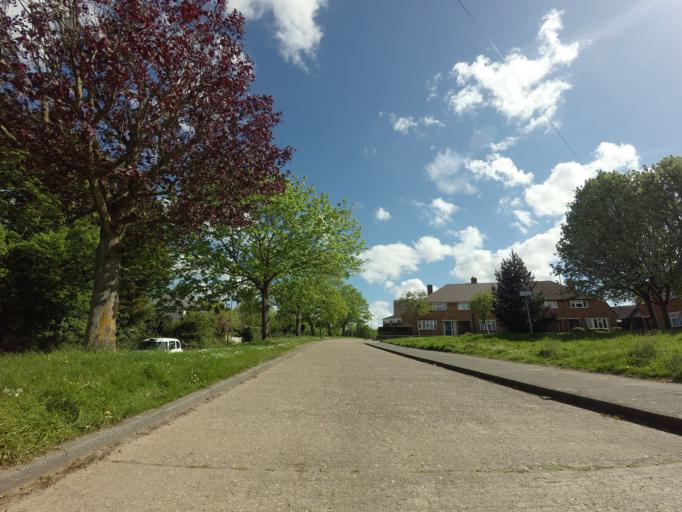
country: GB
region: England
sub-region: Greater London
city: Orpington
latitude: 51.3776
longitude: 0.1220
